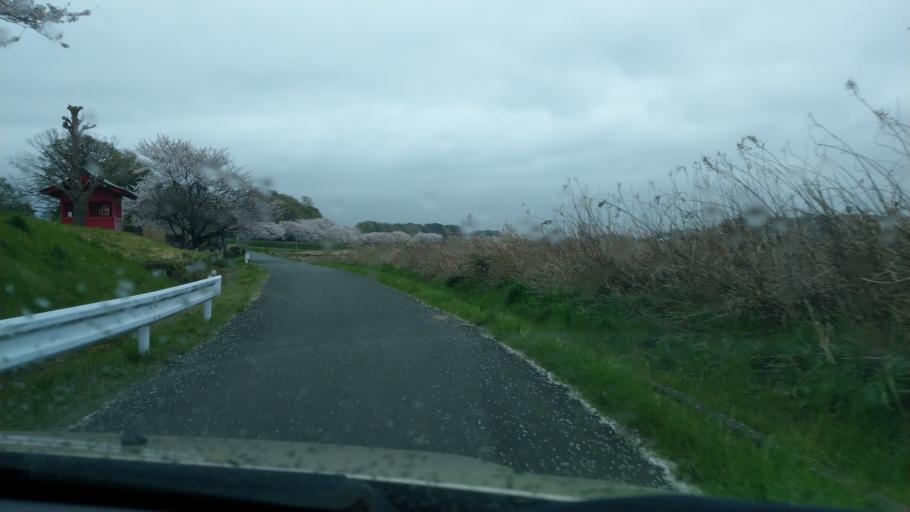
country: JP
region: Saitama
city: Saitama
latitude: 35.9171
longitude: 139.6872
